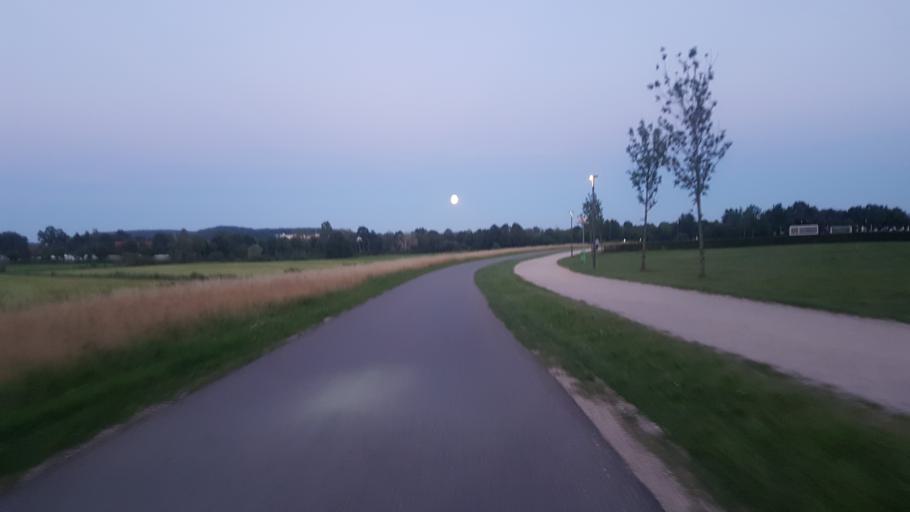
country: DE
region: Bavaria
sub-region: Regierungsbezirk Mittelfranken
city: Gunzenhausen
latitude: 49.1287
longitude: 10.7370
